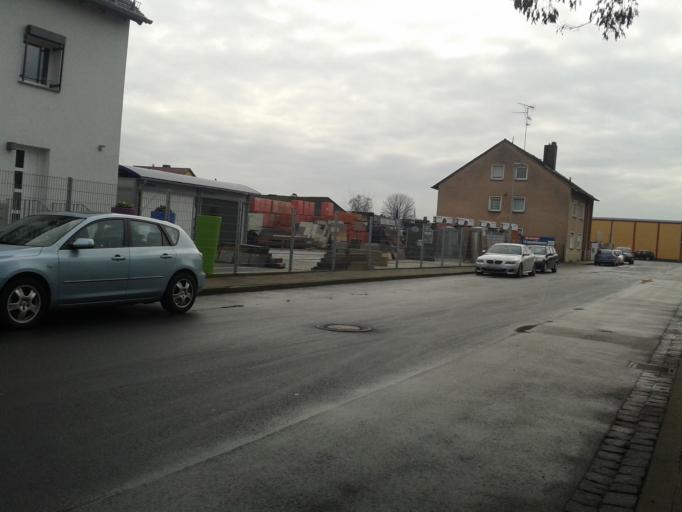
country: DE
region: Bavaria
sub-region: Upper Franconia
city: Hallstadt
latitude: 49.9113
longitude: 10.8827
